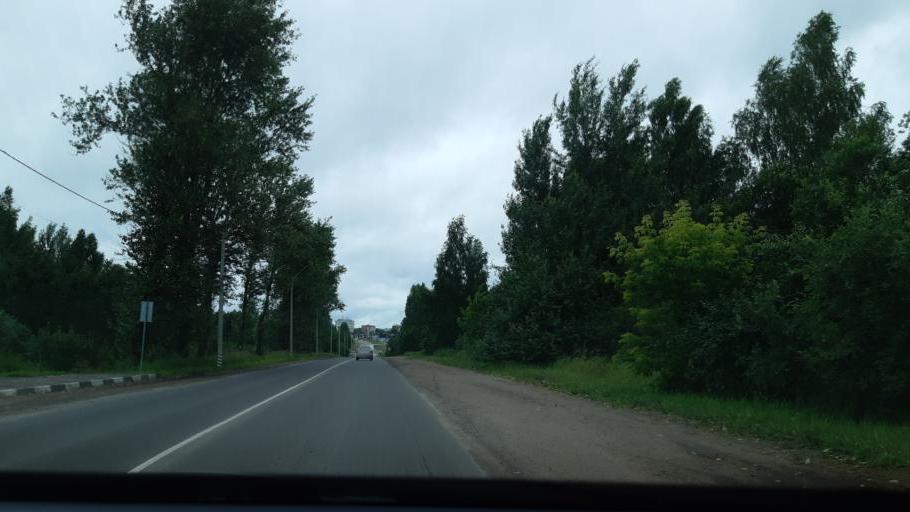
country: RU
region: Smolensk
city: Desnogorsk
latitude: 54.1365
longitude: 33.2777
